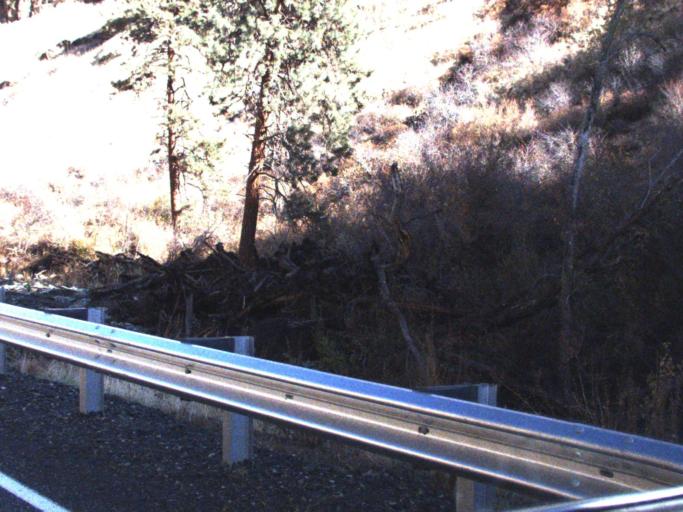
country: US
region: Washington
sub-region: Asotin County
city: Asotin
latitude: 46.0449
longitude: -117.2441
